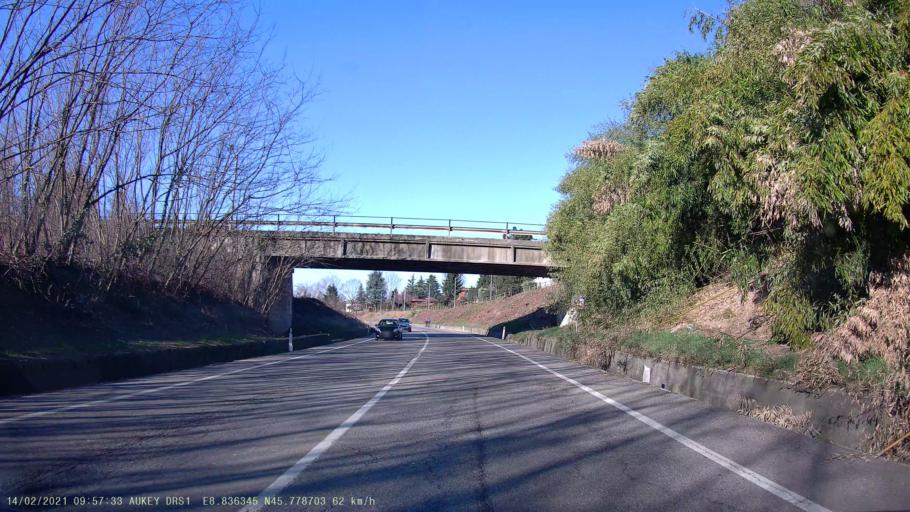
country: IT
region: Lombardy
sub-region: Provincia di Varese
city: Gazzada Schianno
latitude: 45.7787
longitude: 8.8357
